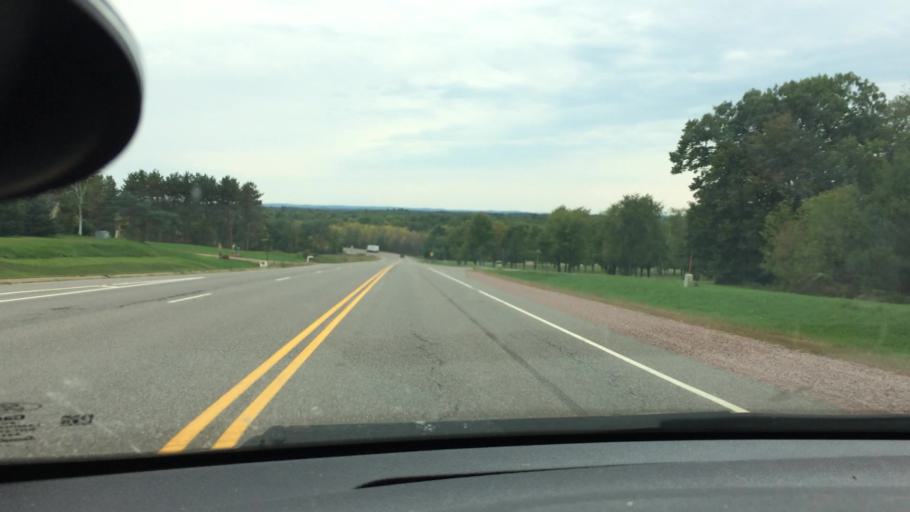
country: US
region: Wisconsin
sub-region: Clark County
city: Neillsville
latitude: 44.5660
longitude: -90.6683
